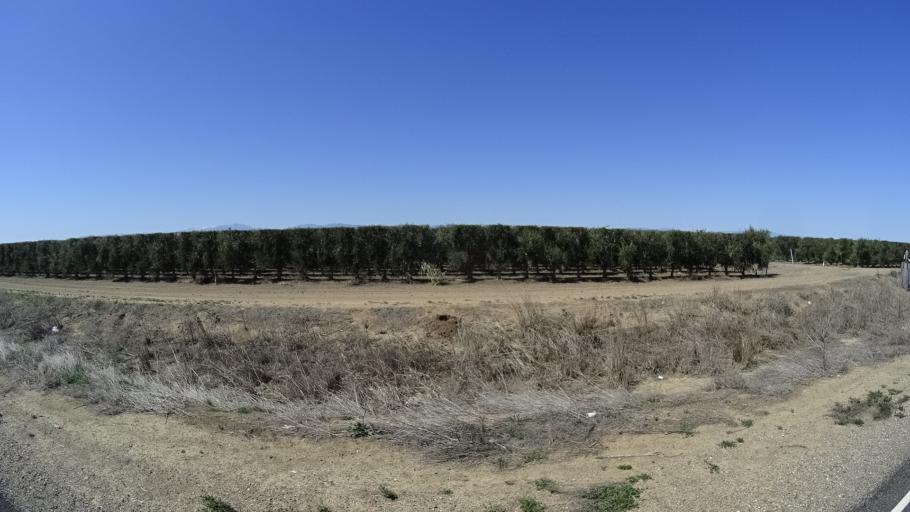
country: US
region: California
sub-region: Glenn County
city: Willows
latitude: 39.5991
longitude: -122.2498
